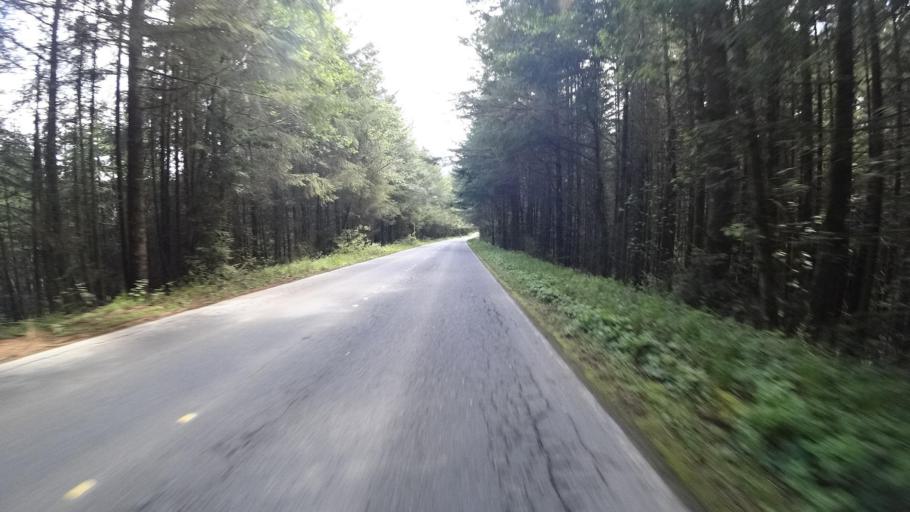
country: US
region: California
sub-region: Humboldt County
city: McKinleyville
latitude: 40.9703
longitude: -124.0523
